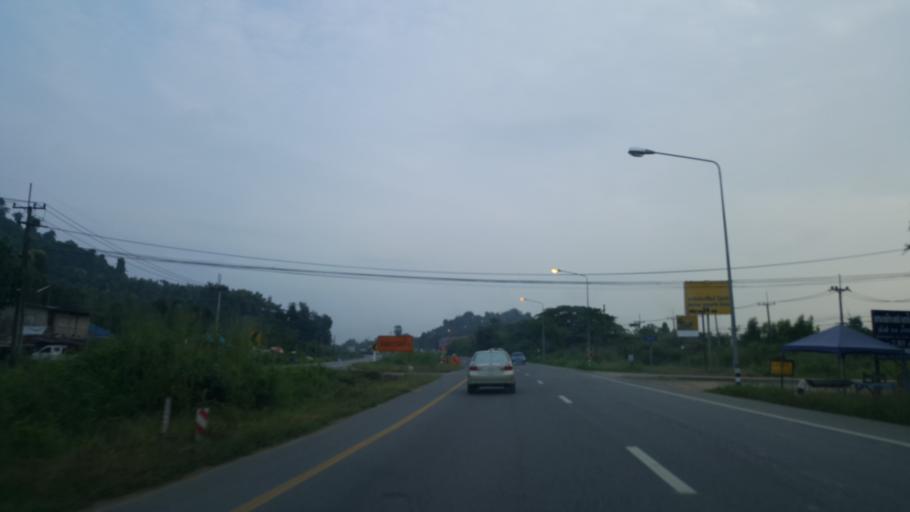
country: TH
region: Rayong
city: Ban Chang
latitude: 12.7376
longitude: 100.9895
